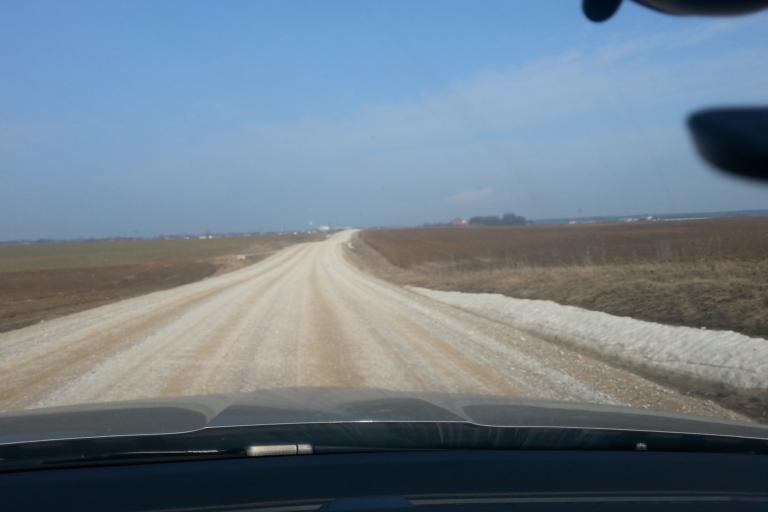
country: LT
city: Trakai
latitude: 54.5949
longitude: 24.9777
